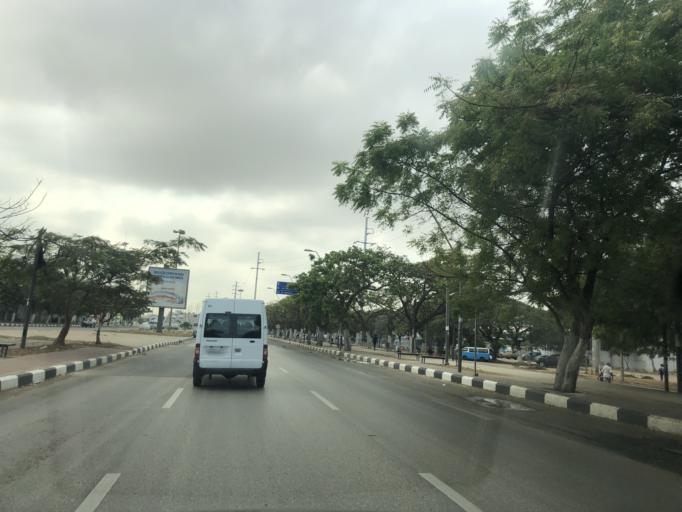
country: AO
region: Luanda
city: Luanda
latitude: -8.8326
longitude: 13.2526
